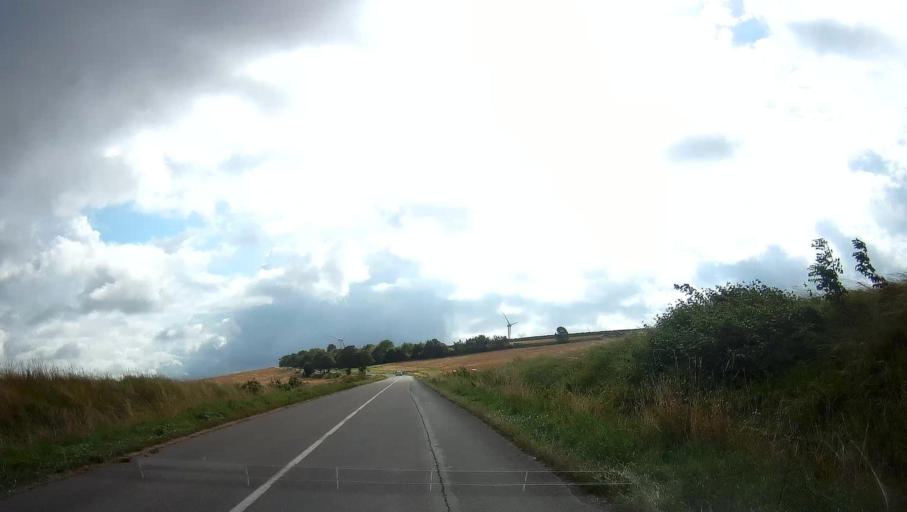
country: FR
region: Champagne-Ardenne
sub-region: Departement des Ardennes
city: Chateau-Porcien
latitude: 49.5383
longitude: 4.2978
